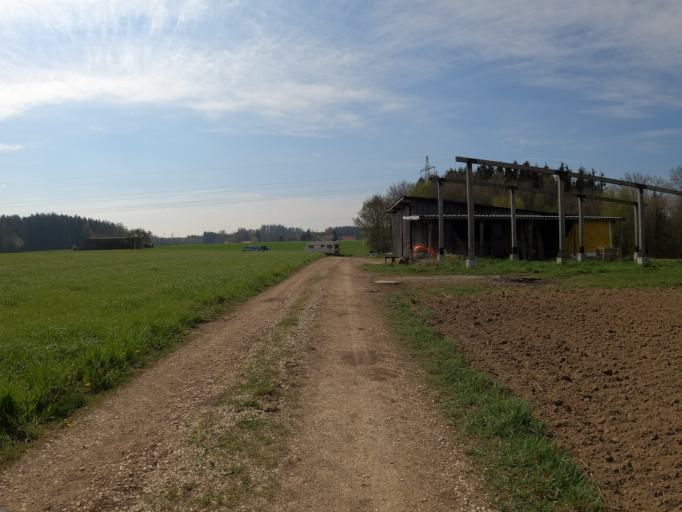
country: DE
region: Bavaria
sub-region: Swabia
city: Rieden an der Kotz
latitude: 48.3754
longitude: 10.2176
